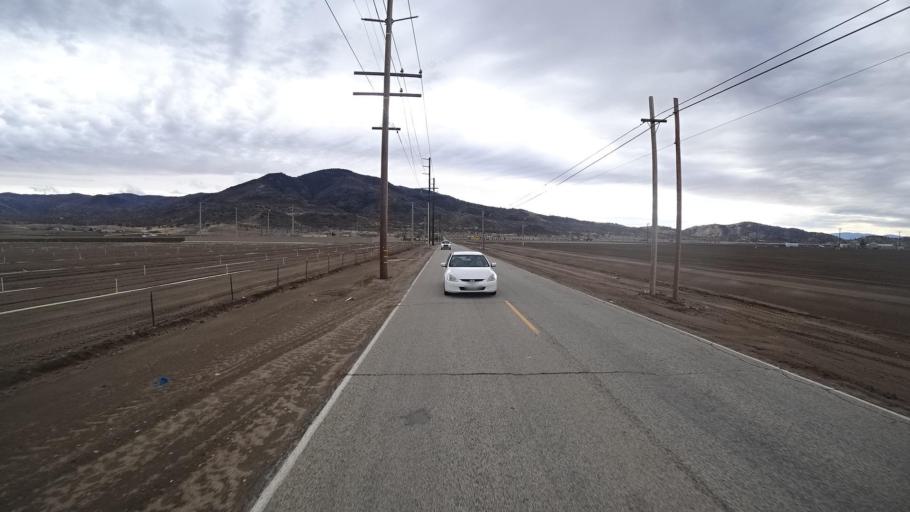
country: US
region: California
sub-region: Kern County
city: Stallion Springs
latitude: 35.1030
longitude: -118.6020
